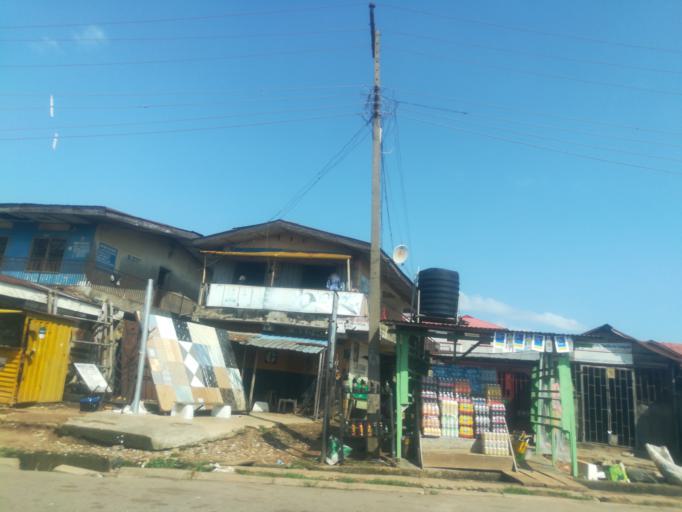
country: NG
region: Oyo
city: Ibadan
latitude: 7.4115
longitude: 3.9524
